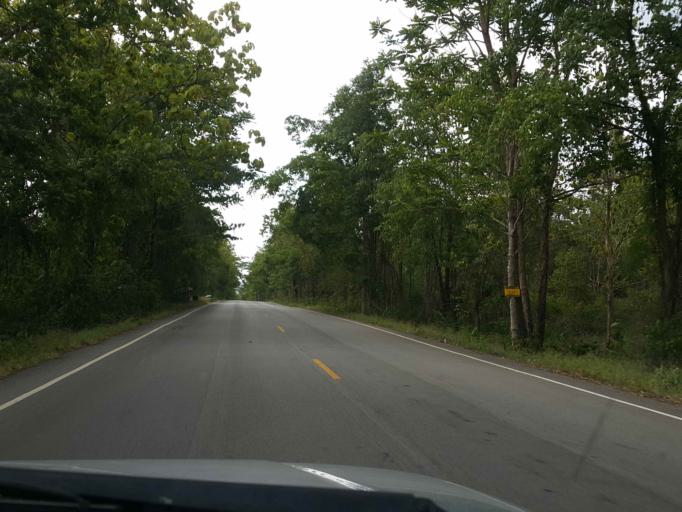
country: TH
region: Sukhothai
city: Thung Saliam
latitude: 17.3920
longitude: 99.3954
